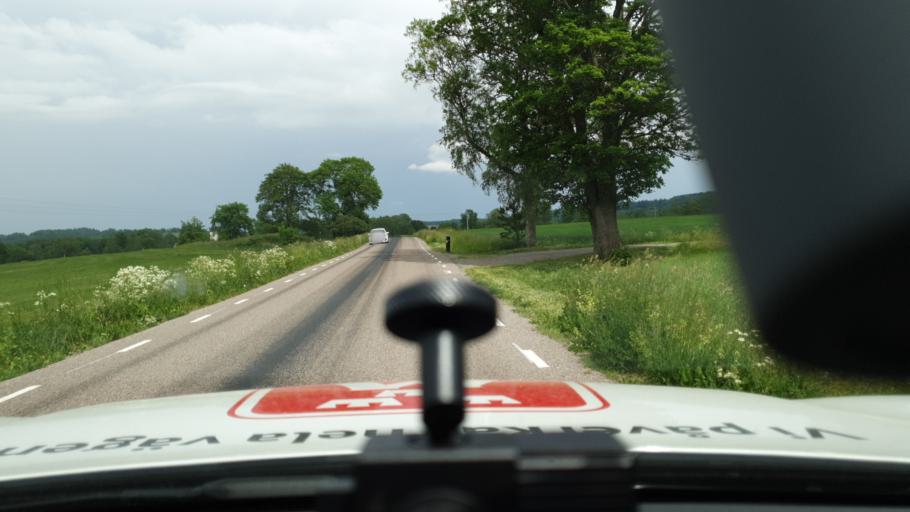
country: SE
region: Vaestra Goetaland
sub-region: Falkopings Kommun
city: Akarp
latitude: 58.1895
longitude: 13.7129
